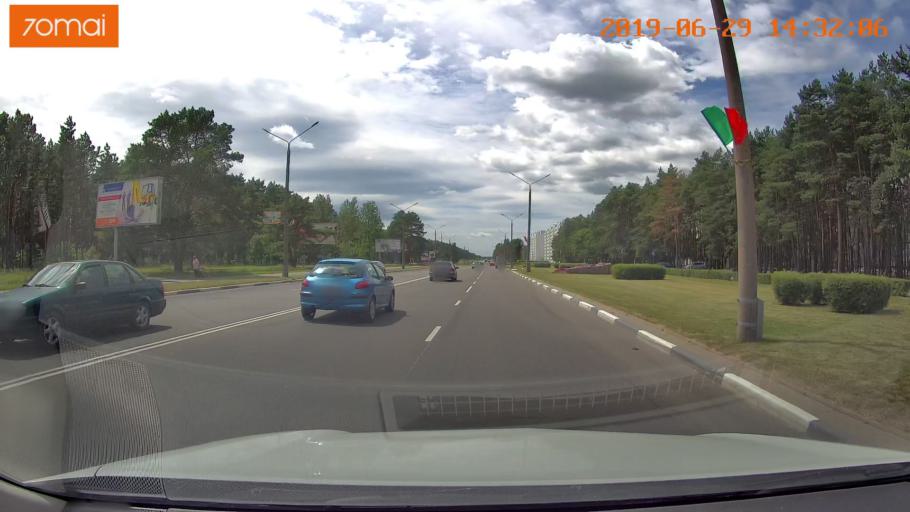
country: BY
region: Minsk
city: Salihorsk
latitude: 52.7815
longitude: 27.5066
